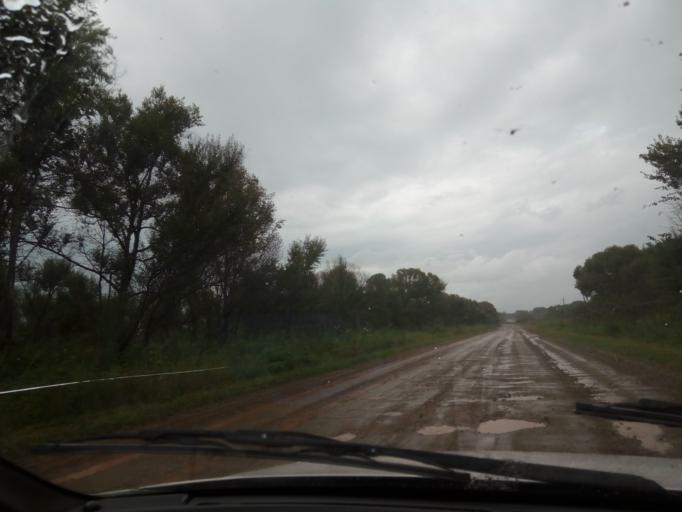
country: RU
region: Primorskiy
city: Lazo
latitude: 45.8488
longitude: 133.6454
